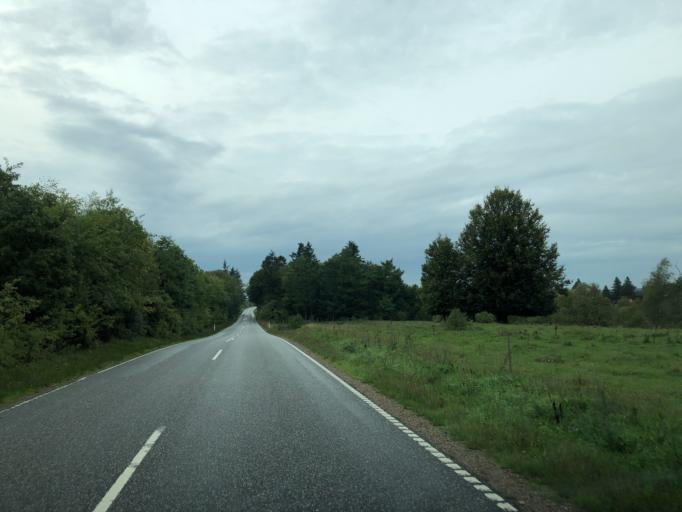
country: DK
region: Central Jutland
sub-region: Ikast-Brande Kommune
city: Brande
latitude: 55.9956
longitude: 9.1993
